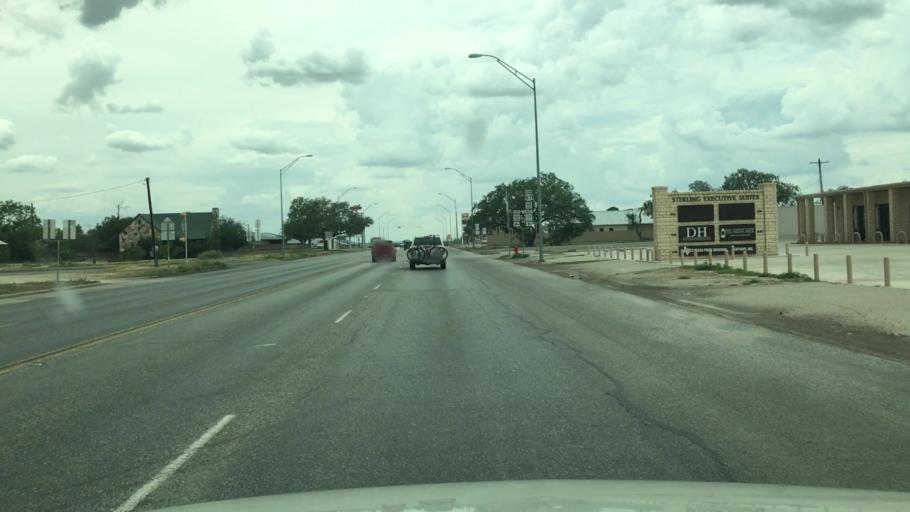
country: US
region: Texas
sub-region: Sterling County
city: Sterling City
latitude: 31.8366
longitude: -100.9910
